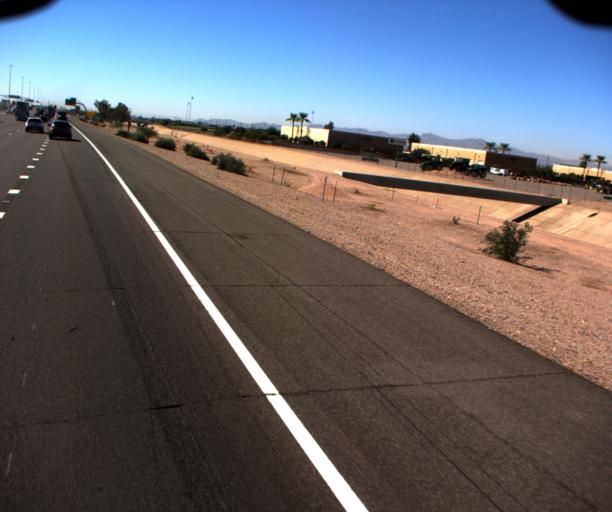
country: US
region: Arizona
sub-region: Maricopa County
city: Tolleson
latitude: 33.4611
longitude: -112.2977
